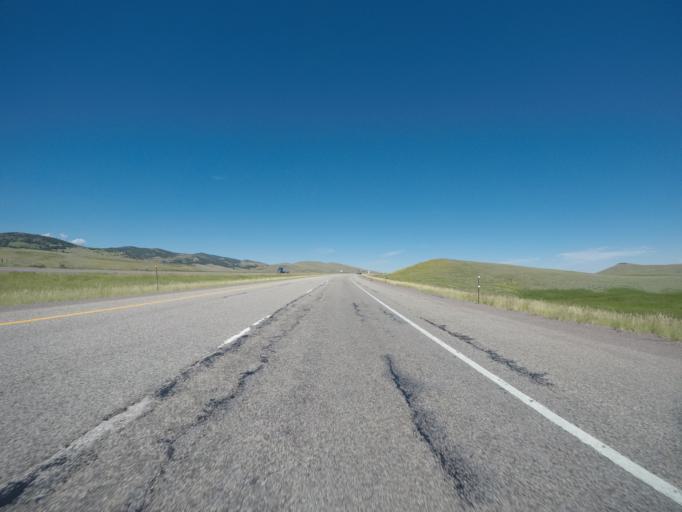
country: US
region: Wyoming
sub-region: Albany County
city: Laramie
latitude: 41.5656
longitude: -106.1386
